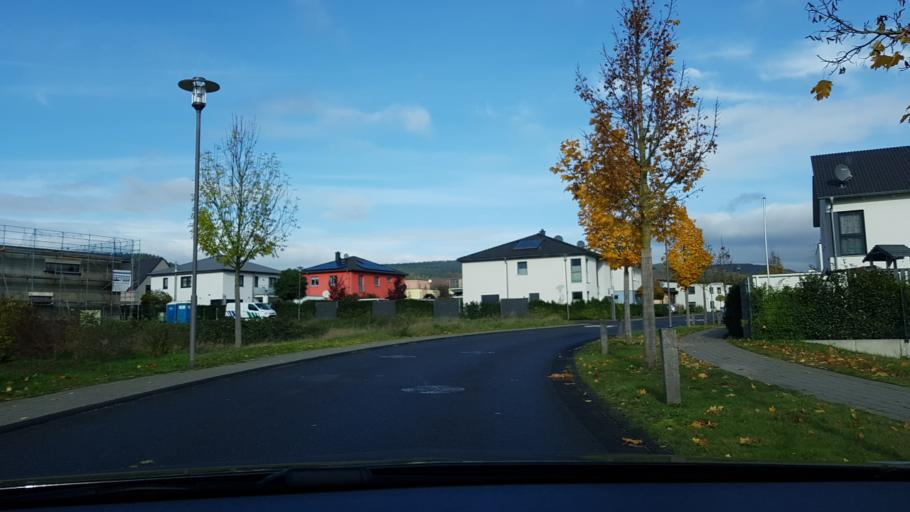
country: DE
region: Rheinland-Pfalz
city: Schweich
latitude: 49.8241
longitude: 6.7396
